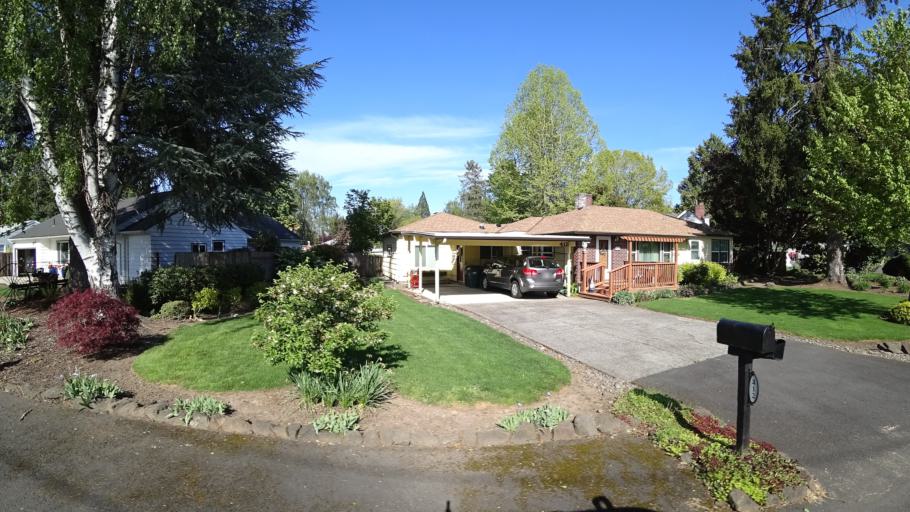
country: US
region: Oregon
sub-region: Washington County
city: Hillsboro
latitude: 45.5265
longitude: -122.9796
